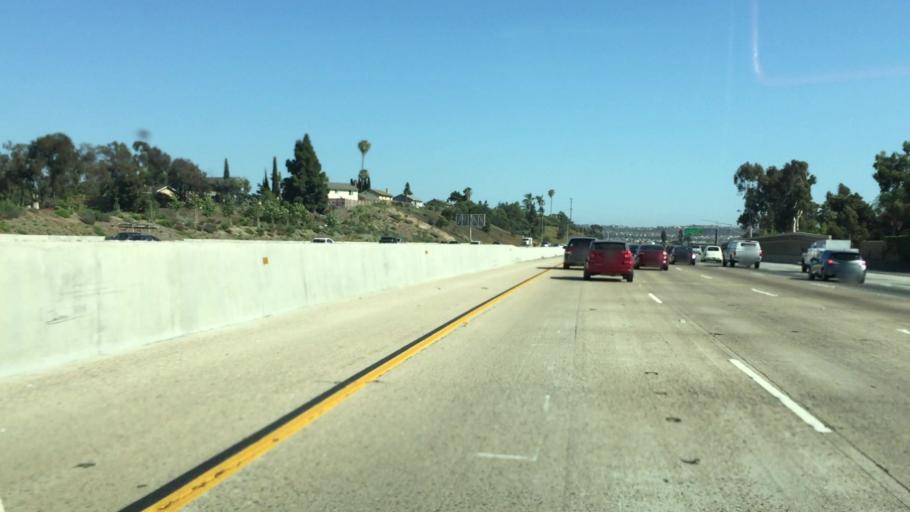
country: US
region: California
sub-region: San Diego County
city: Bonita
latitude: 32.6131
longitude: -117.0374
